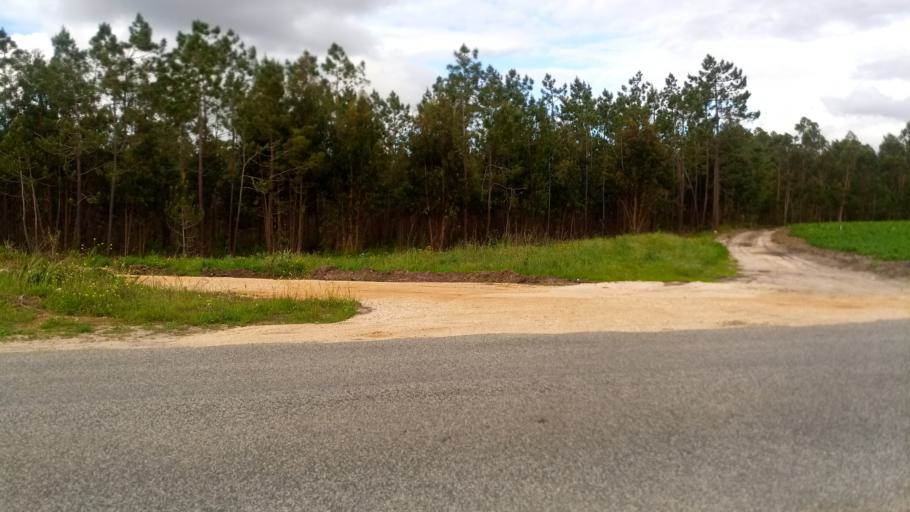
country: PT
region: Leiria
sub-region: Caldas da Rainha
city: Caldas da Rainha
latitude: 39.4441
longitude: -9.1652
